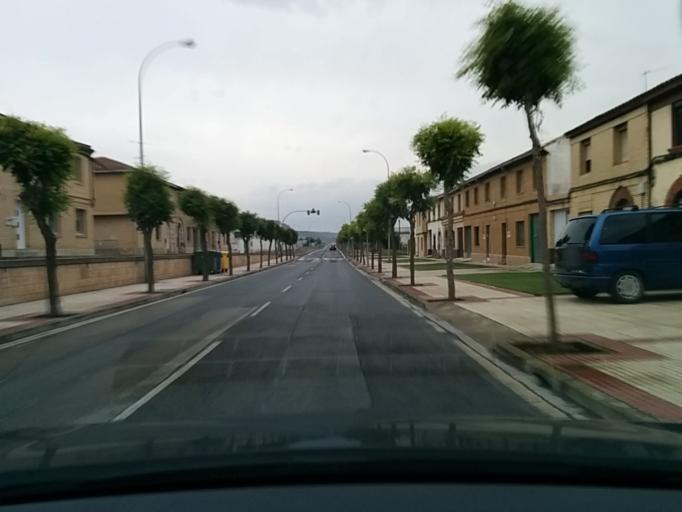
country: ES
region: Navarre
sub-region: Provincia de Navarra
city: Valtierra
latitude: 42.1897
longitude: -1.6256
